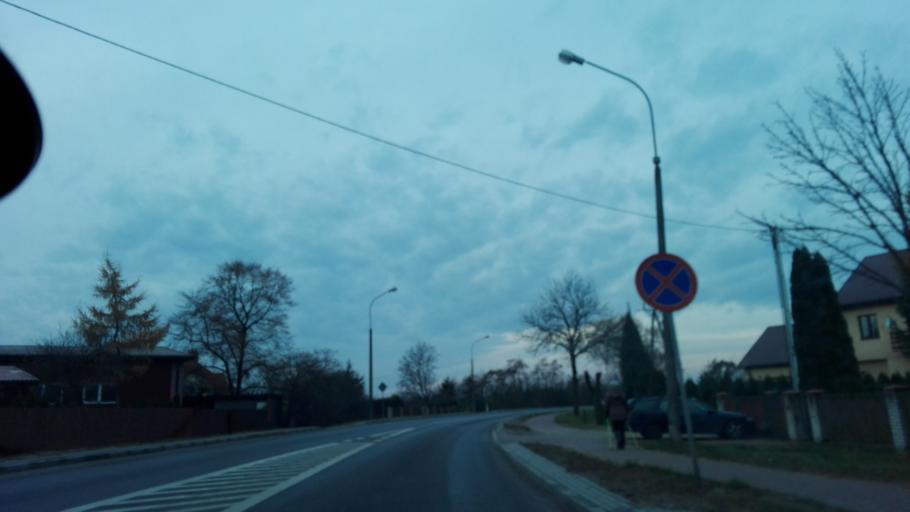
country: PL
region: Lublin Voivodeship
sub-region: Powiat radzynski
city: Radzyn Podlaski
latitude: 51.7726
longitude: 22.6033
